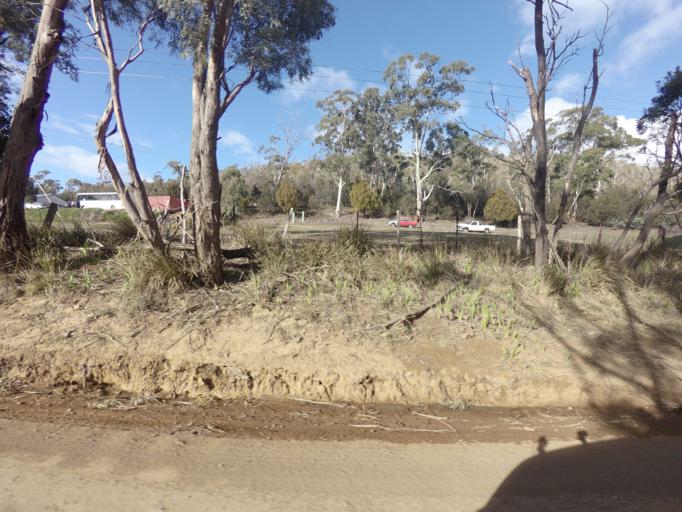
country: AU
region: Tasmania
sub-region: Derwent Valley
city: New Norfolk
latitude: -42.8096
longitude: 147.1325
